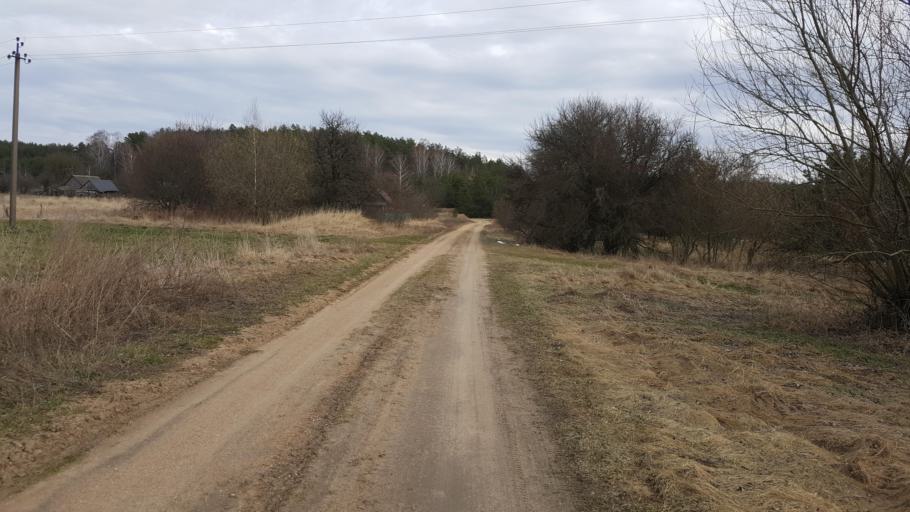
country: BY
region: Brest
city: Kamyanyets
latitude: 52.3739
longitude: 23.9797
